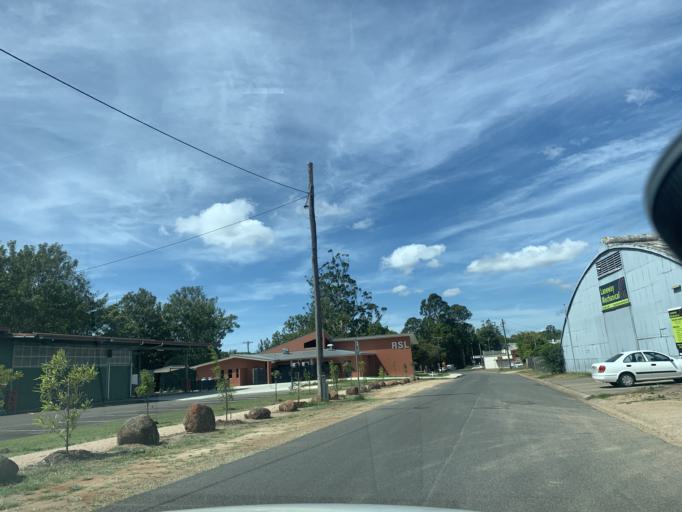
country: AU
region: Queensland
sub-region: Tablelands
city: Atherton
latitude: -17.2638
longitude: 145.4761
